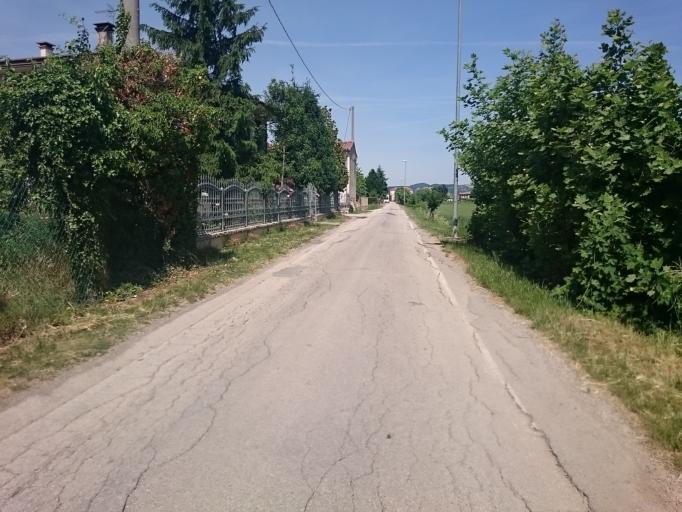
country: IT
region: Veneto
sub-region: Provincia di Padova
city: Lozzo Atestino
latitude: 45.3102
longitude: 11.6034
